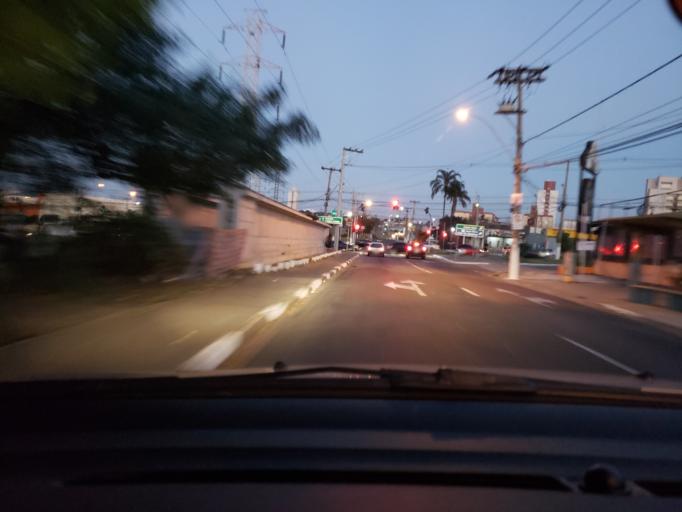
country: BR
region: Sao Paulo
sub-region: Campinas
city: Campinas
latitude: -22.9147
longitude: -47.1030
